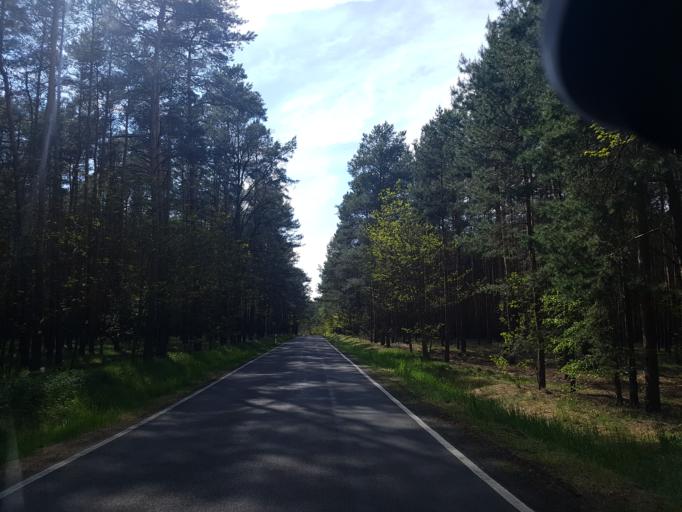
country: DE
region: Brandenburg
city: Heinersbruck
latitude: 51.6871
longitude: 14.5013
